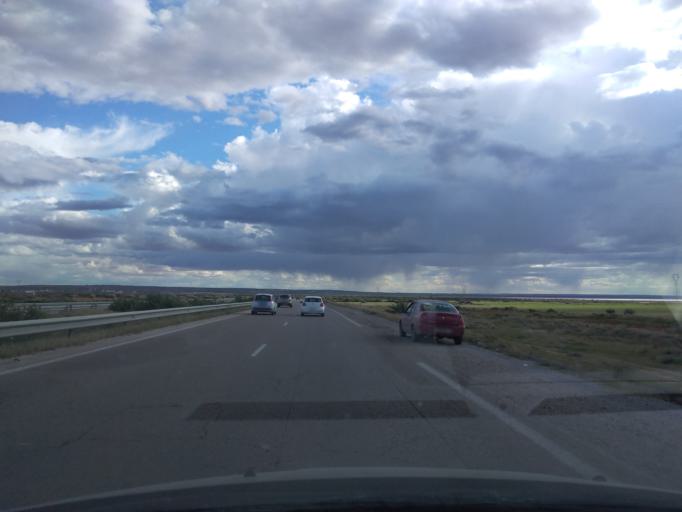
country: TN
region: Al Munastir
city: Manzil Kamil
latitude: 35.5053
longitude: 10.6254
